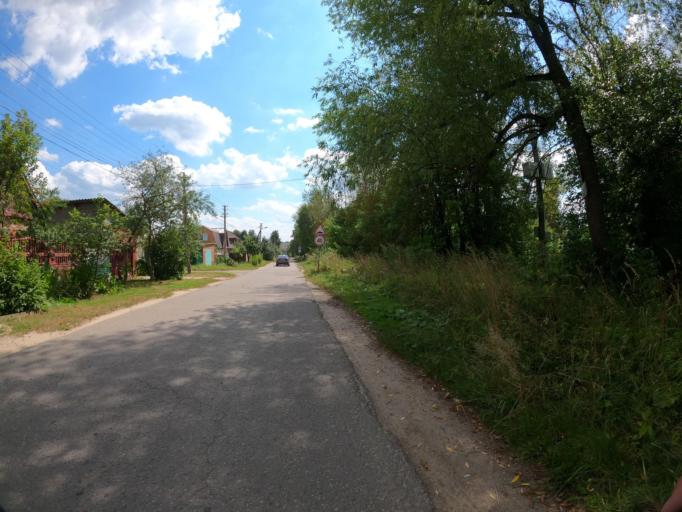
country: RU
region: Moskovskaya
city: Lopatinskiy
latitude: 55.2805
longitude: 38.7439
